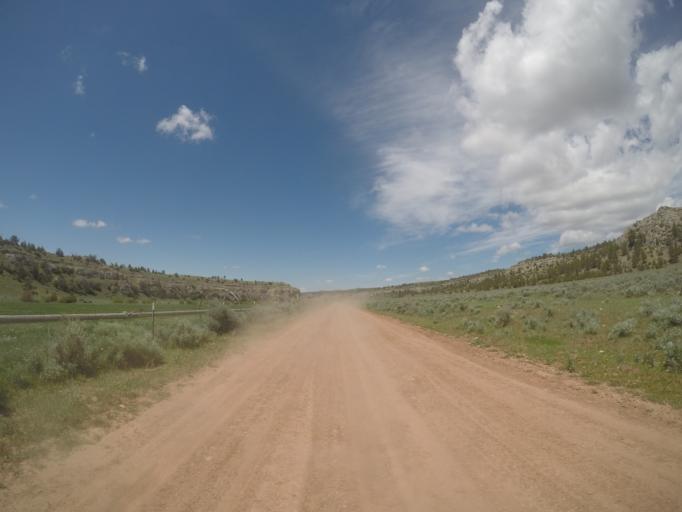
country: US
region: Montana
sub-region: Yellowstone County
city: Laurel
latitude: 45.2395
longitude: -108.6330
